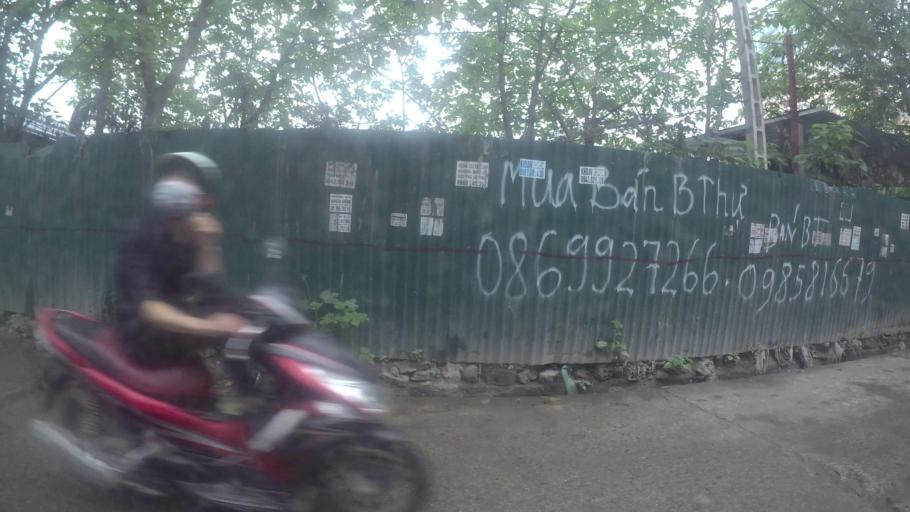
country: VN
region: Ha Noi
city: Cau Giay
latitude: 21.0232
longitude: 105.7872
